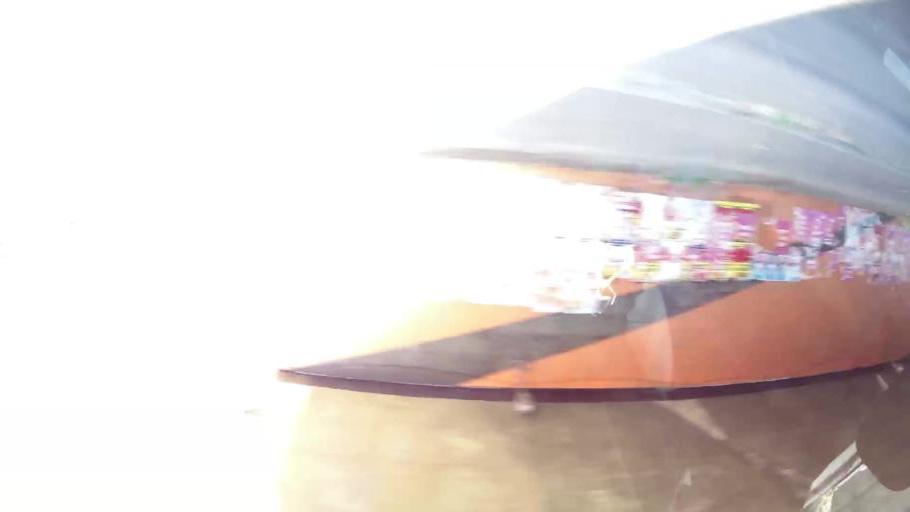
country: ZA
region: Orange Free State
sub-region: Mangaung Metropolitan Municipality
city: Bloemfontein
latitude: -29.1195
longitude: 26.2306
